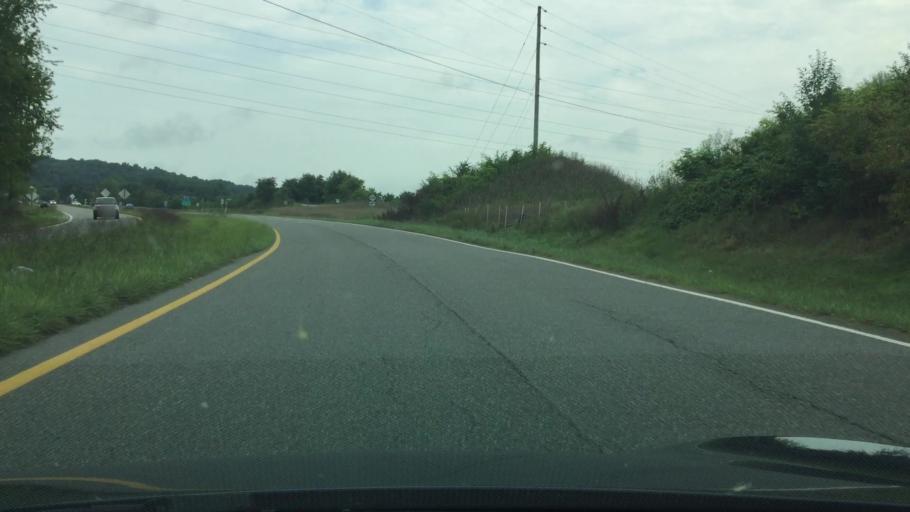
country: US
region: Virginia
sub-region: City of Radford
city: Radford
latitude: 37.0918
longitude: -80.5064
